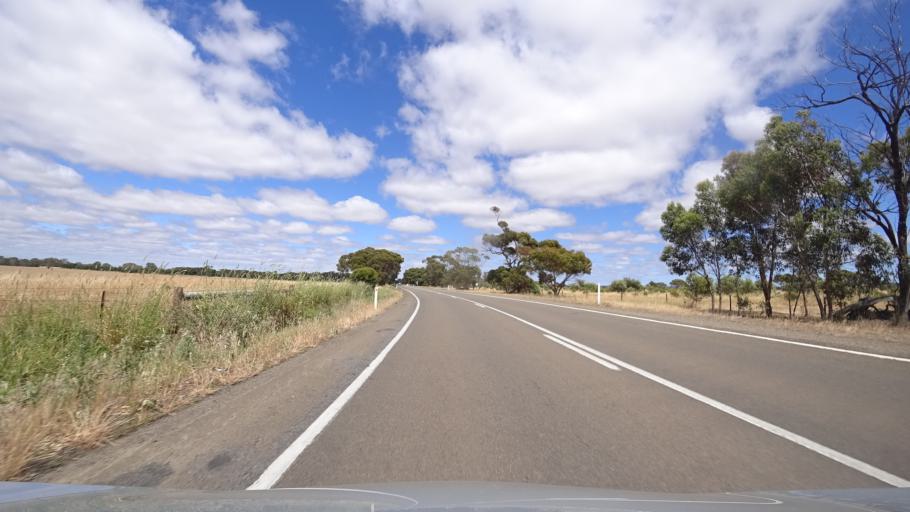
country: AU
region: South Australia
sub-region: Kangaroo Island
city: Kingscote
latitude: -35.6824
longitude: 137.5488
